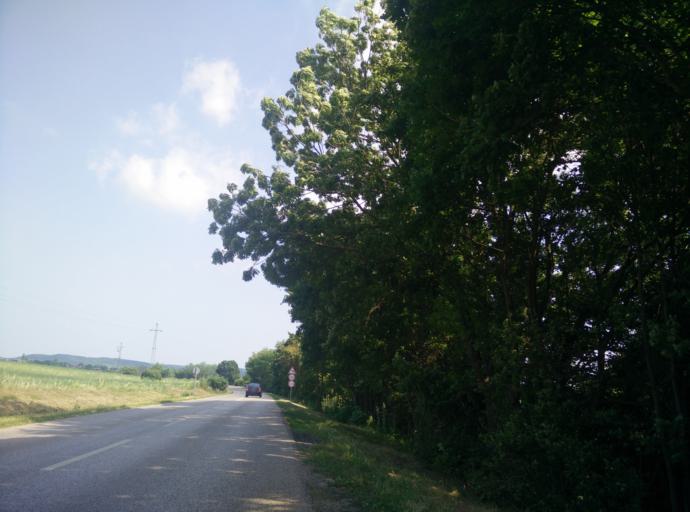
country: HU
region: Pest
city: Biatorbagy
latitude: 47.4754
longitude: 18.7939
